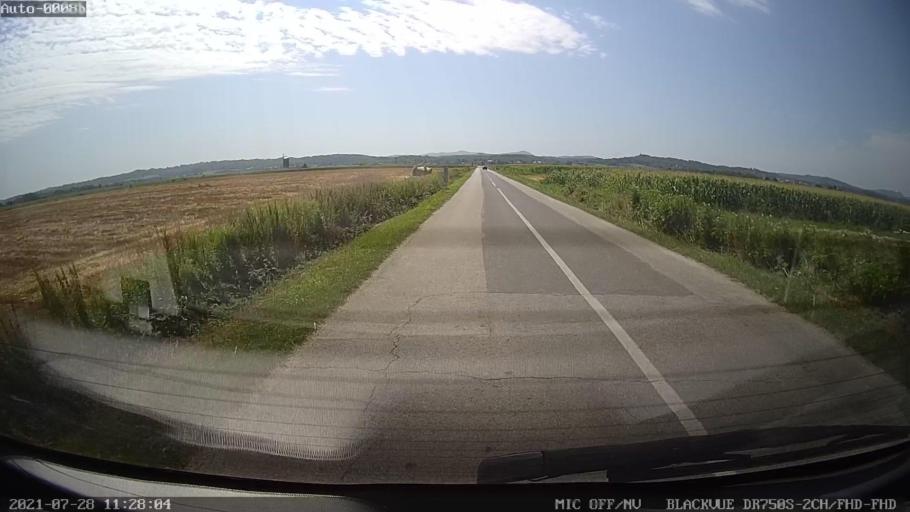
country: HR
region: Varazdinska
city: Jalzabet
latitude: 46.2744
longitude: 16.4337
